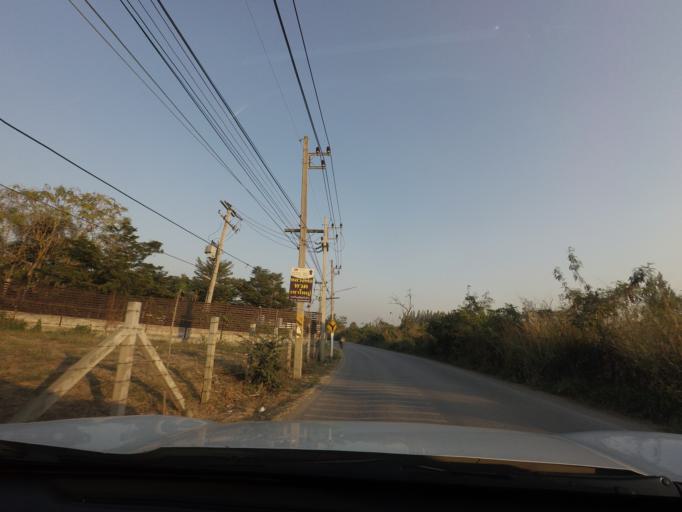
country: TH
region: Nakhon Ratchasima
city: Pak Chong
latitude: 14.6378
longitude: 101.4270
